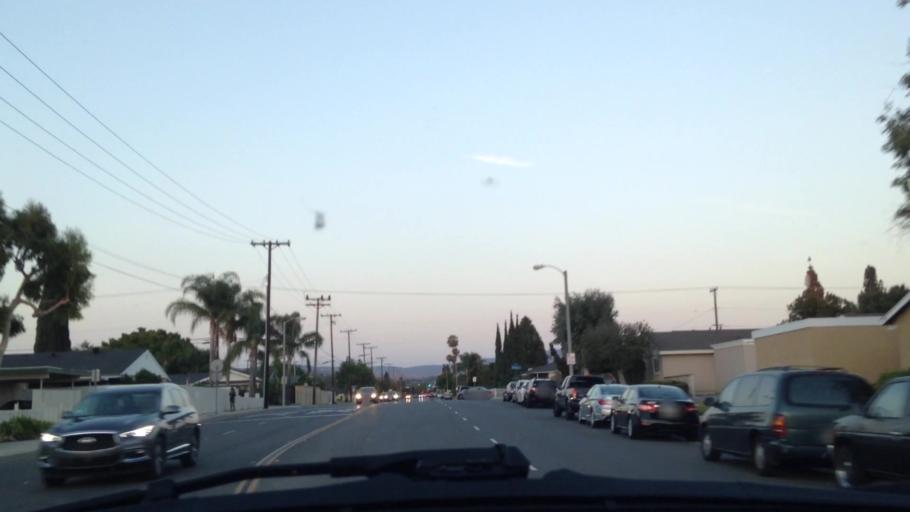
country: US
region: California
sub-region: Orange County
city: Orange
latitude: 33.8230
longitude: -117.8502
